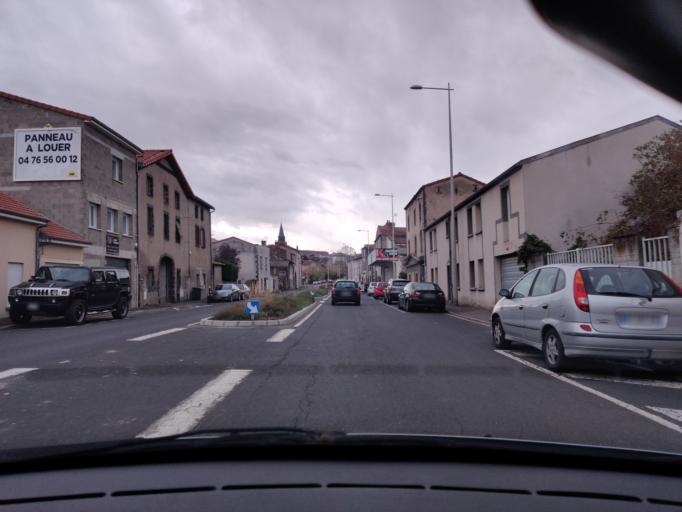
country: FR
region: Auvergne
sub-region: Departement du Puy-de-Dome
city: Riom
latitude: 45.8992
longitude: 3.1163
